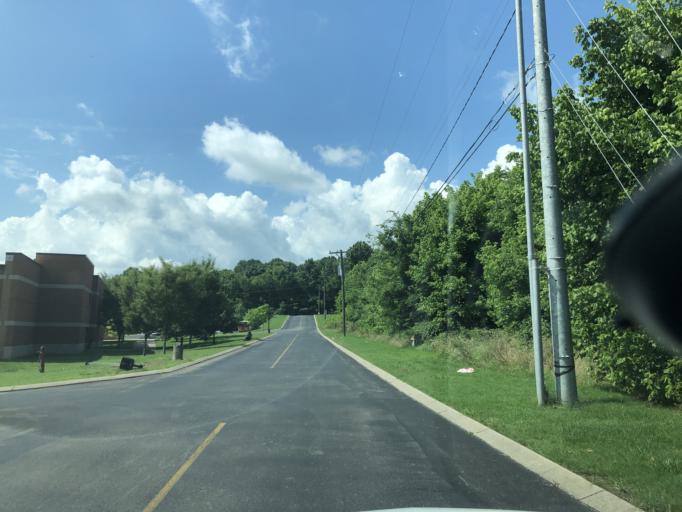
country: US
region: Tennessee
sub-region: Rutherford County
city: La Vergne
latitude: 36.0307
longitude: -86.6225
